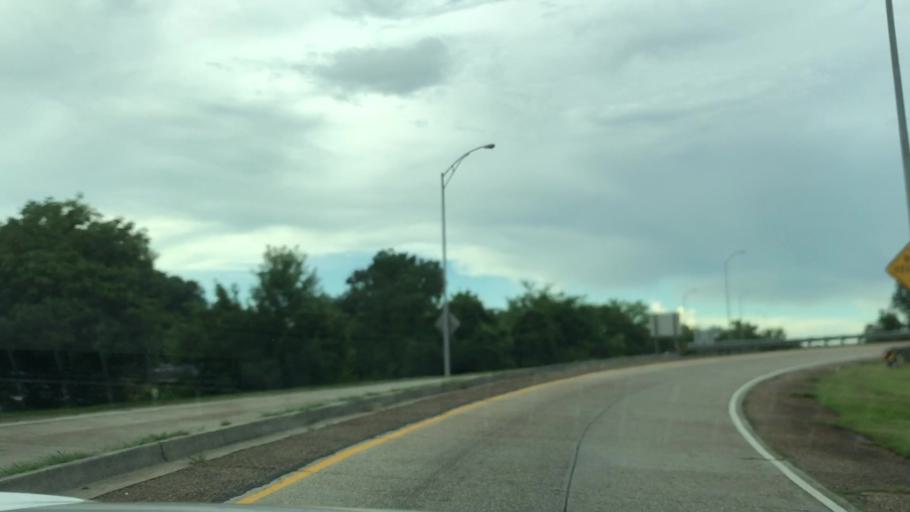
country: US
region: Louisiana
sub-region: East Baton Rouge Parish
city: Brownsfield
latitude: 30.5220
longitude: -91.1634
